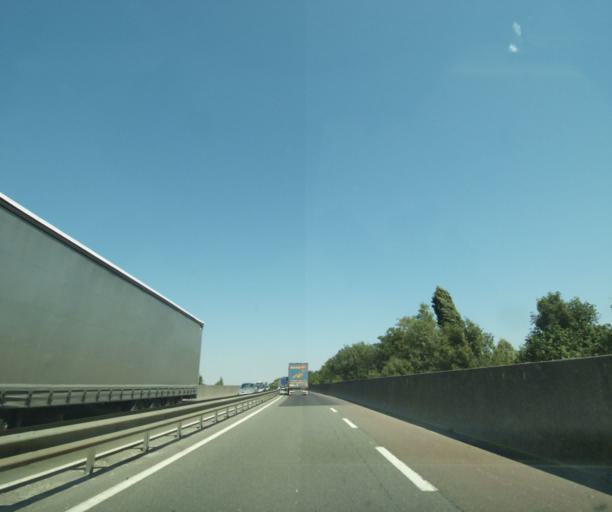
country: FR
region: Champagne-Ardenne
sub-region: Departement de la Haute-Marne
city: Saint-Dizier
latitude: 48.6367
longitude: 4.9216
